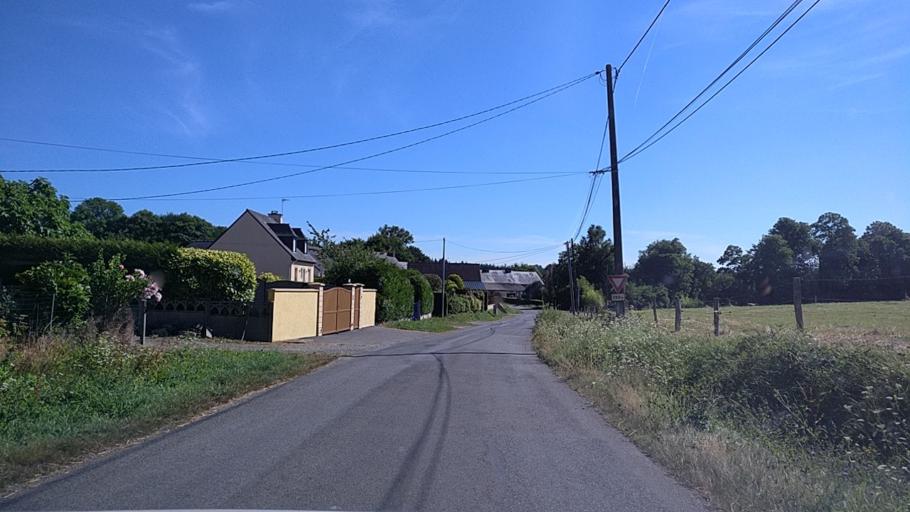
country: FR
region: Brittany
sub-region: Departement d'Ille-et-Vilaine
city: Plerguer
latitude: 48.5174
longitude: -1.8570
